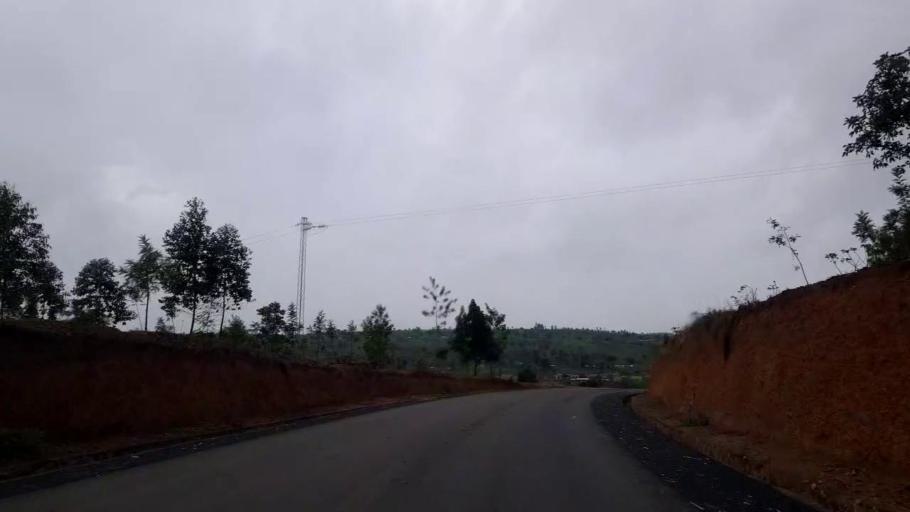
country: RW
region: Northern Province
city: Byumba
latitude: -1.4240
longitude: 30.2712
